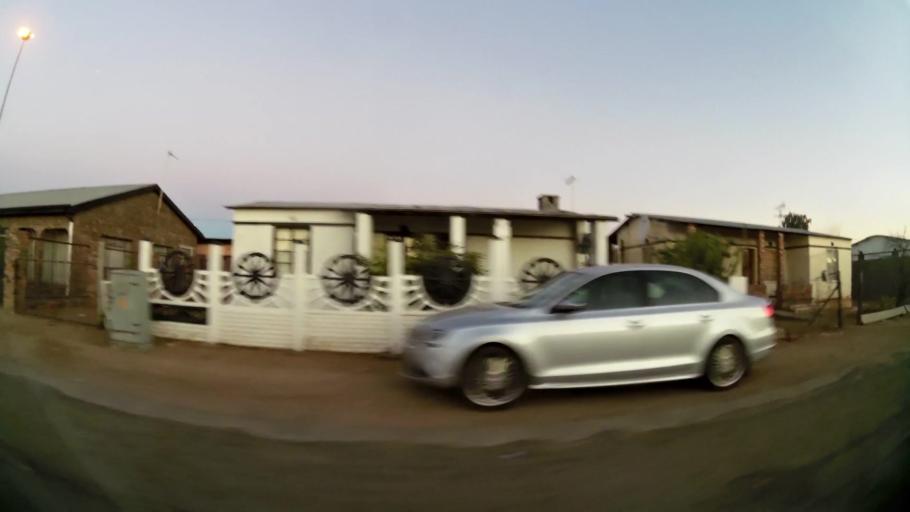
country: ZA
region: Northern Cape
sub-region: Frances Baard District Municipality
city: Kimberley
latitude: -28.7136
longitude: 24.7650
